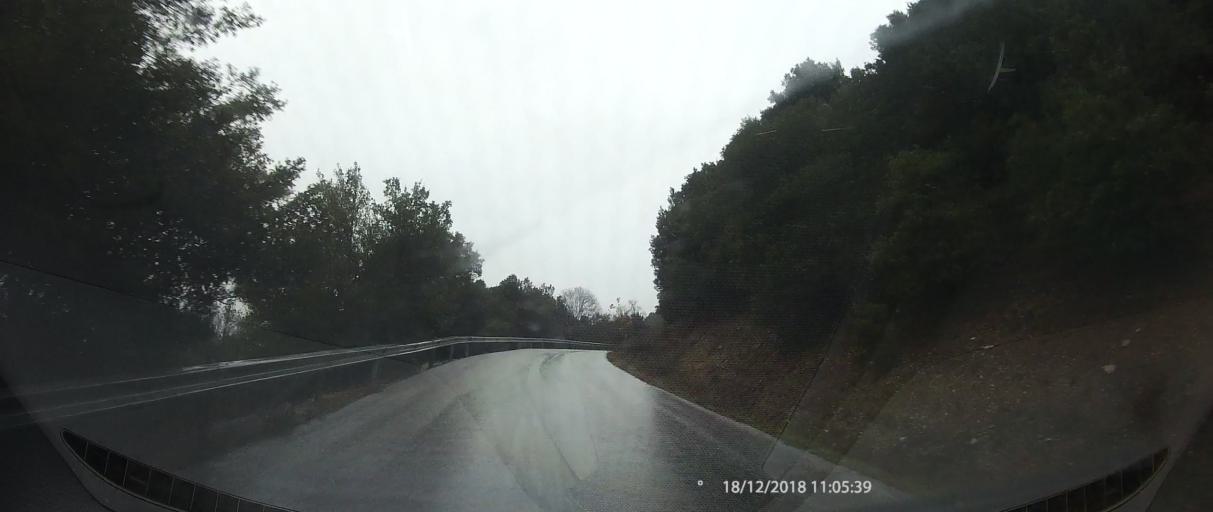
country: GR
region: Central Macedonia
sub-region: Nomos Pierias
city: Kato Milia
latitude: 40.2146
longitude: 22.3207
